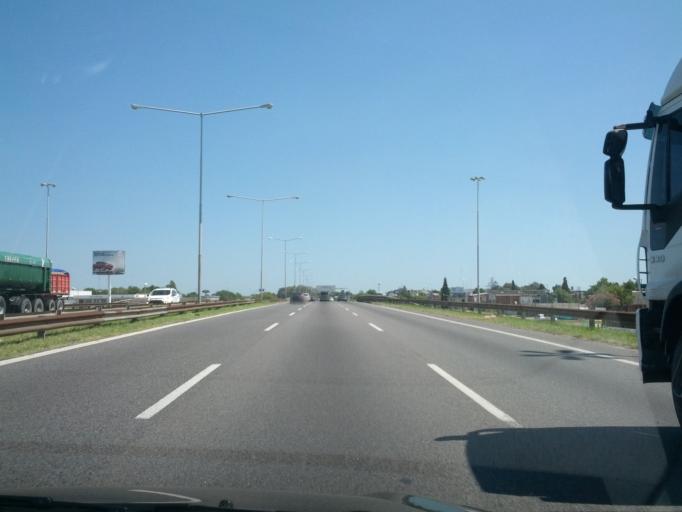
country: AR
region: Buenos Aires
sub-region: Partido de Campana
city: Campana
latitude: -34.1911
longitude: -58.9435
